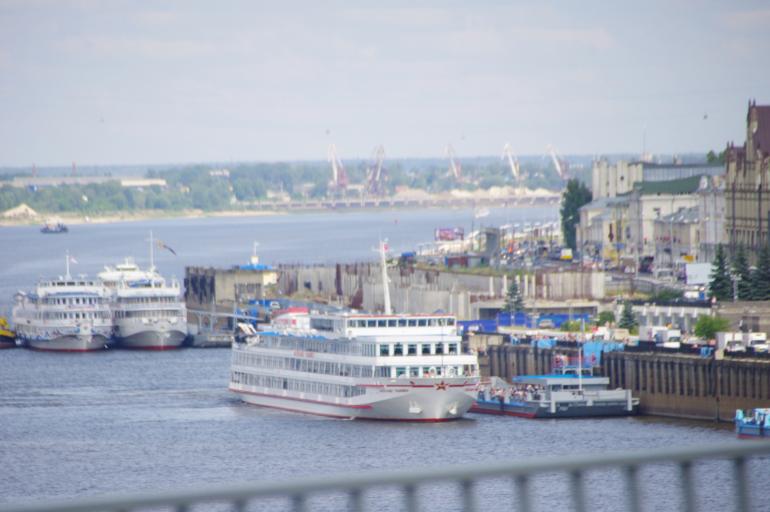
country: RU
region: Nizjnij Novgorod
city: Nizhniy Novgorod
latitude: 56.3276
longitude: 43.9734
